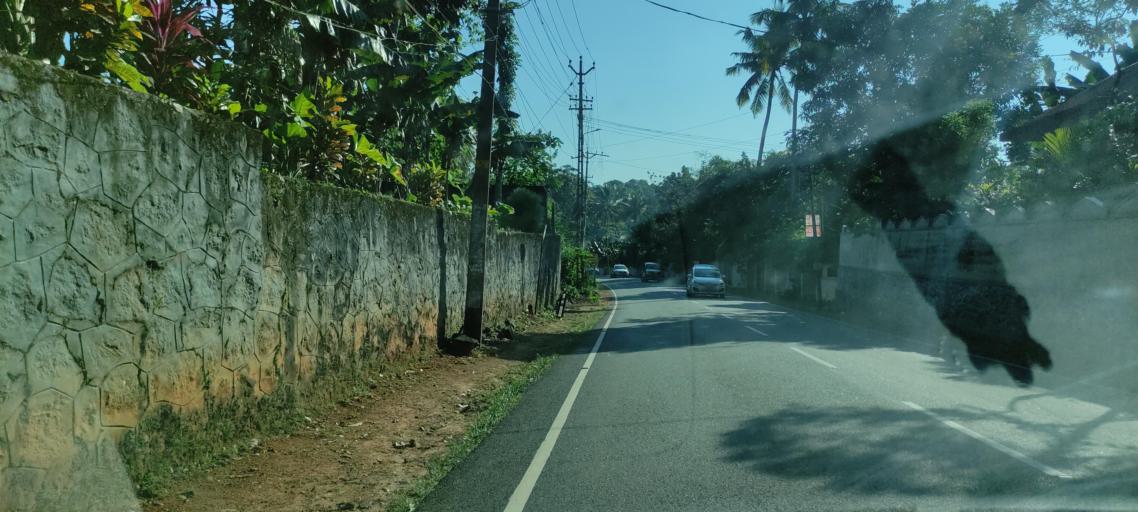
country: IN
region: Kerala
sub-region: Pattanamtitta
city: Pathanamthitta
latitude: 9.2275
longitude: 76.7539
